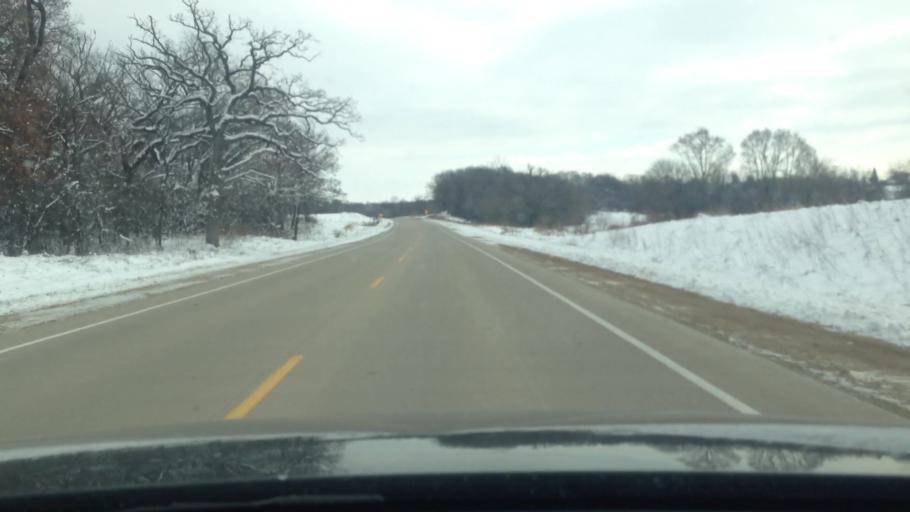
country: US
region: Wisconsin
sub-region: Walworth County
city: Lake Geneva
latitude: 42.5455
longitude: -88.4352
